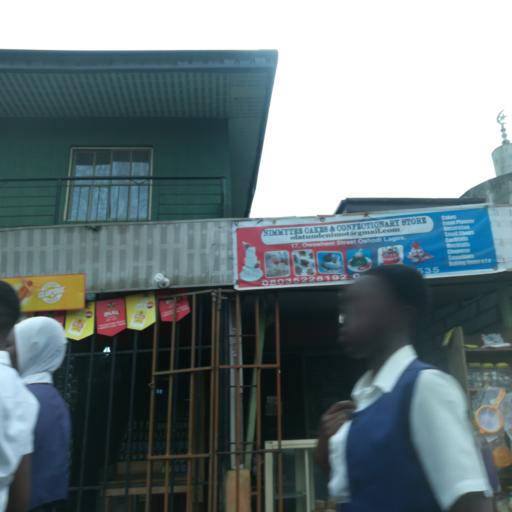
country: NG
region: Lagos
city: Oshodi
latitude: 6.5589
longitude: 3.3445
